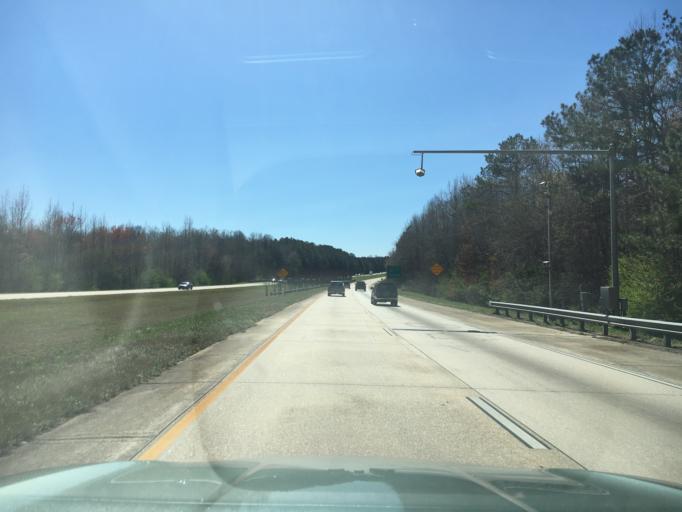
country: US
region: Georgia
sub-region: Troup County
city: Hogansville
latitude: 33.0996
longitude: -84.9076
